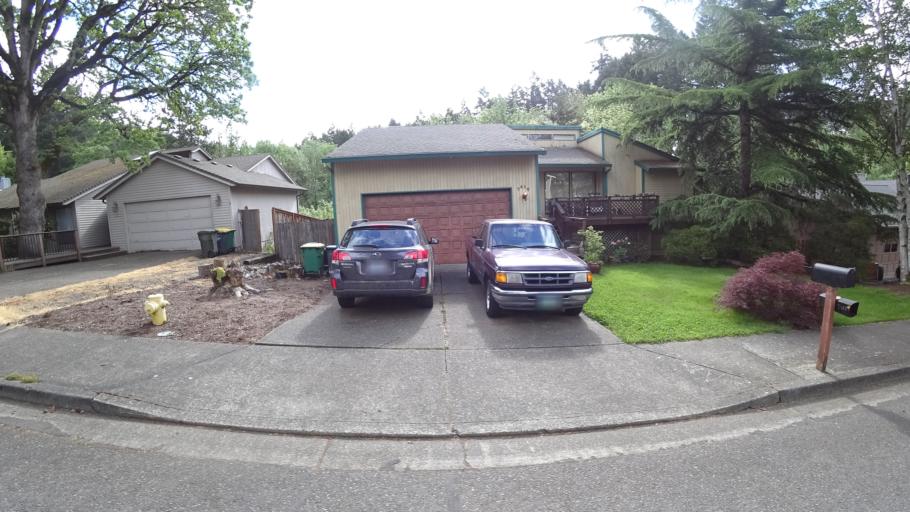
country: US
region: Oregon
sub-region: Washington County
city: Beaverton
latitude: 45.4663
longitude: -122.8344
